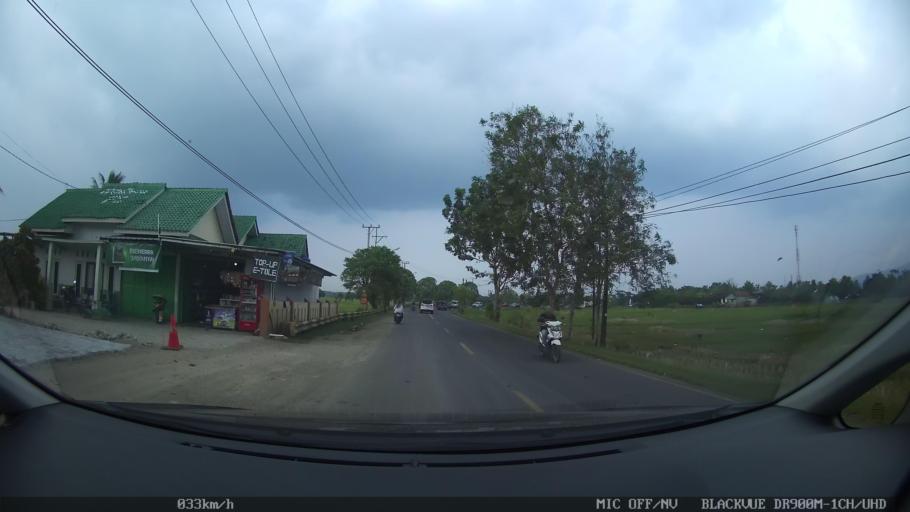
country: ID
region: Lampung
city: Gadingrejo
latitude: -5.3718
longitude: 105.0724
